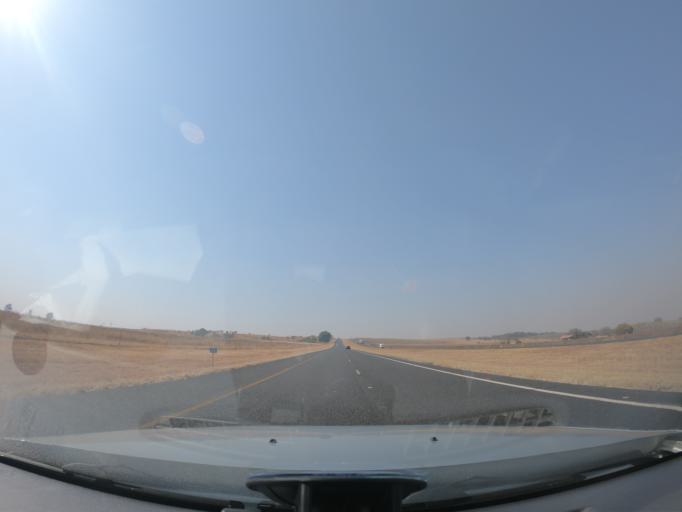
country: ZA
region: Gauteng
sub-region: City of Tshwane Metropolitan Municipality
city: Bronkhorstspruit
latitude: -25.8703
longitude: 28.9203
